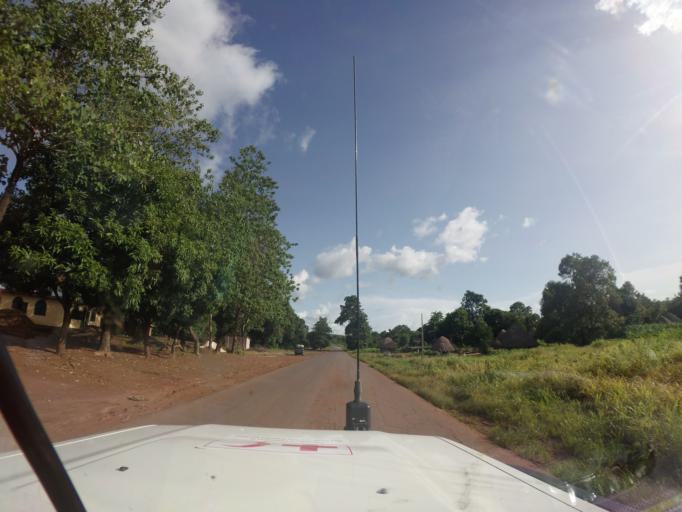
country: GN
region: Kindia
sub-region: Kindia
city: Kindia
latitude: 10.1009
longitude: -12.5649
